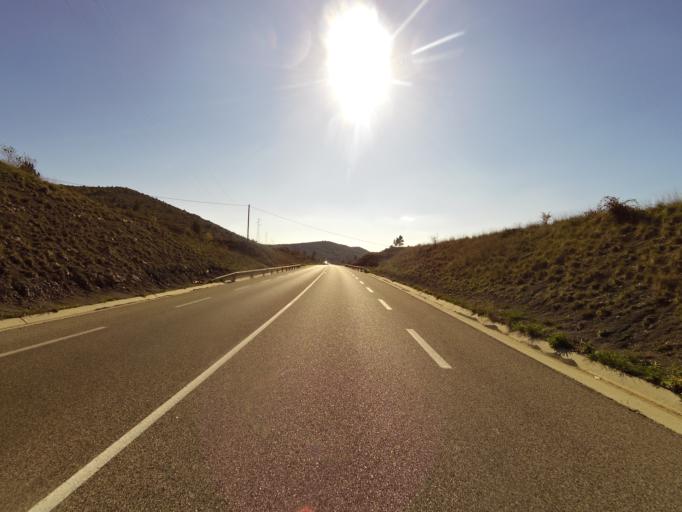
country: FR
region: Rhone-Alpes
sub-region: Departement de l'Ardeche
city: Lachapelle-sous-Aubenas
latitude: 44.5534
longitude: 4.3590
